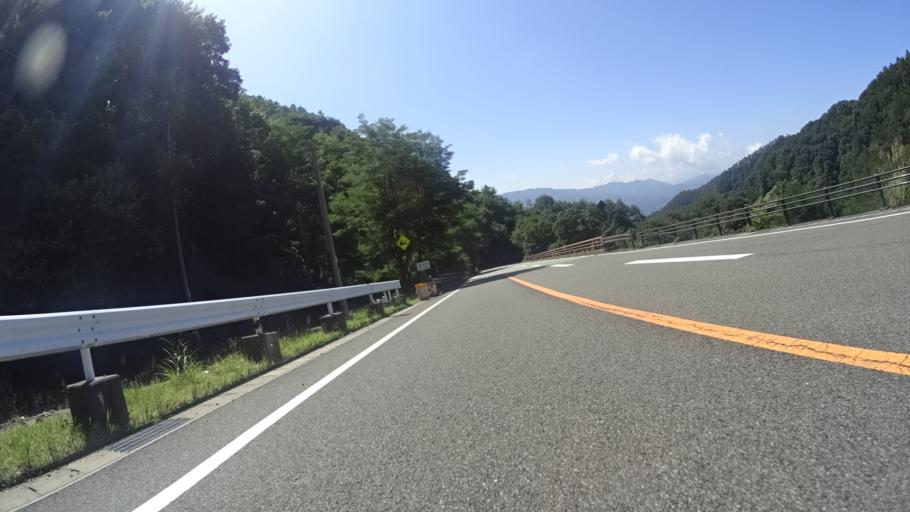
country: JP
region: Yamanashi
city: Enzan
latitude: 35.7630
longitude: 138.8065
